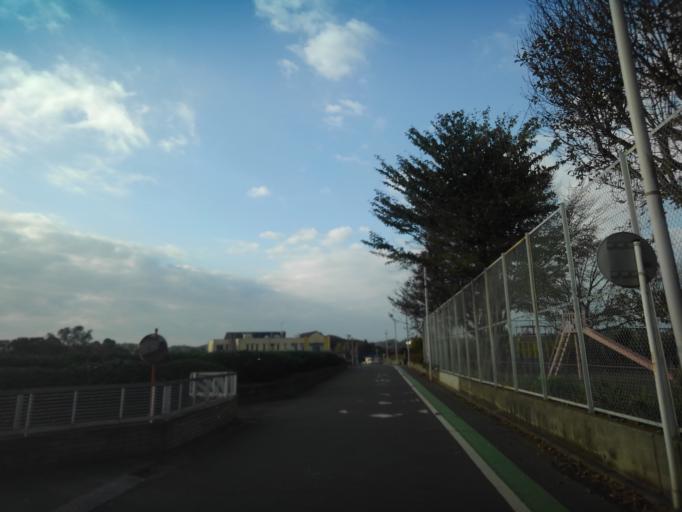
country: JP
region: Saitama
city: Tokorozawa
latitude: 35.7956
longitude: 139.4257
